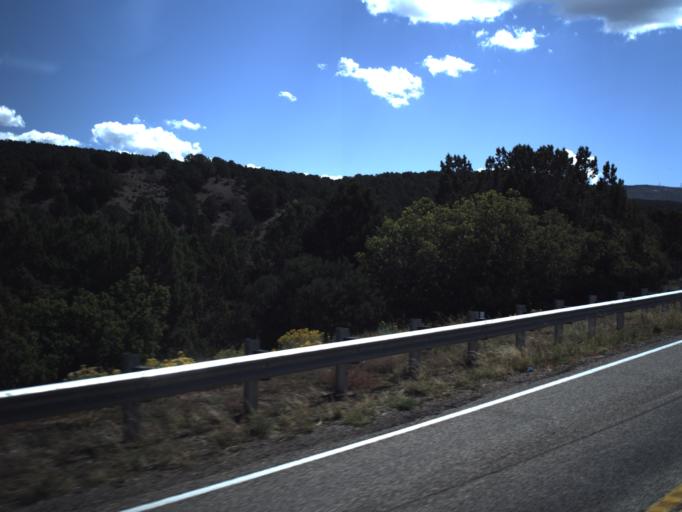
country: US
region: Utah
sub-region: Washington County
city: Enterprise
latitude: 37.5588
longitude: -113.6910
